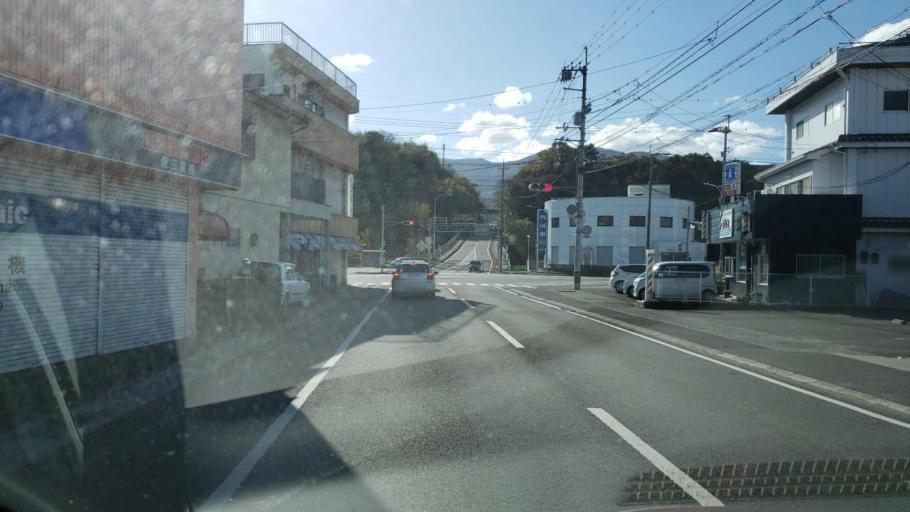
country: JP
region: Tokushima
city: Wakimachi
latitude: 34.0577
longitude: 134.2385
